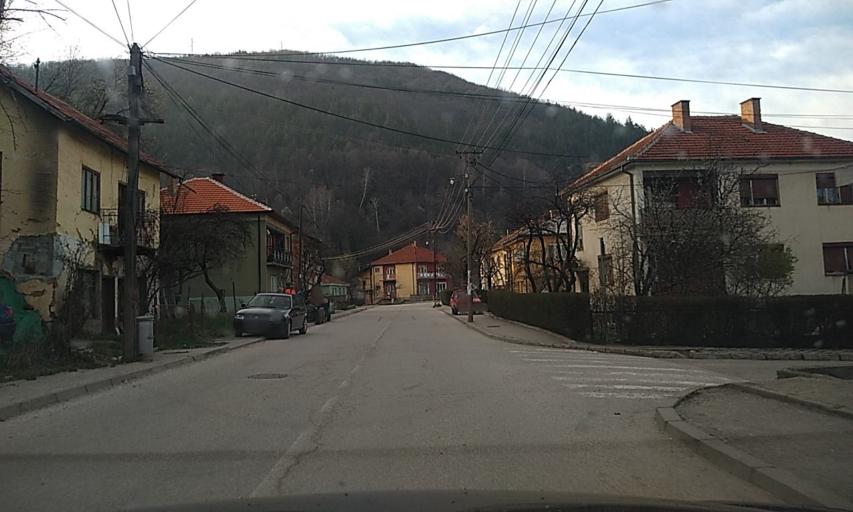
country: RS
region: Central Serbia
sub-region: Pcinjski Okrug
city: Bosilegrad
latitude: 42.4978
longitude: 22.4690
